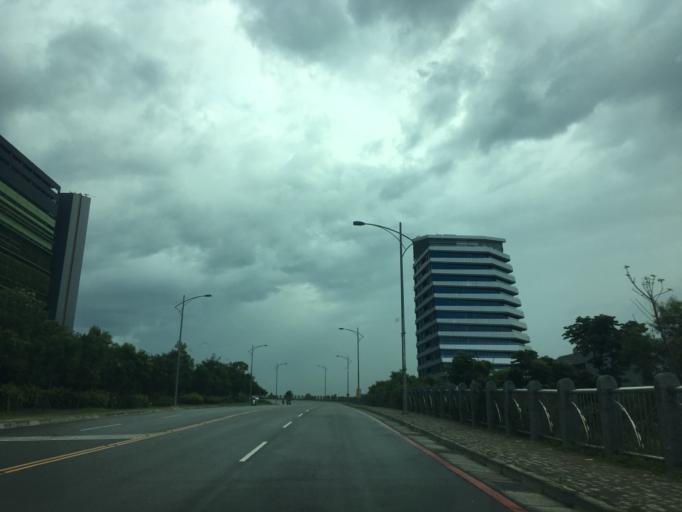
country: TW
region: Taiwan
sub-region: Taichung City
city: Taichung
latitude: 24.2078
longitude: 120.6104
